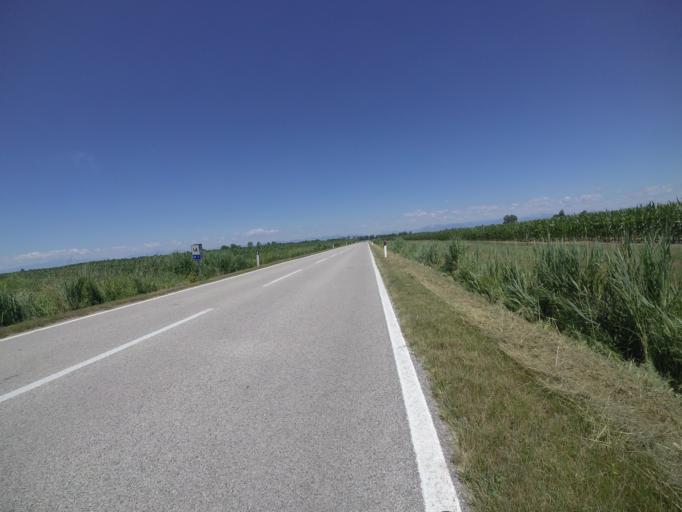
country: IT
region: Friuli Venezia Giulia
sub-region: Provincia di Udine
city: Rivignano
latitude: 45.9007
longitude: 13.0817
